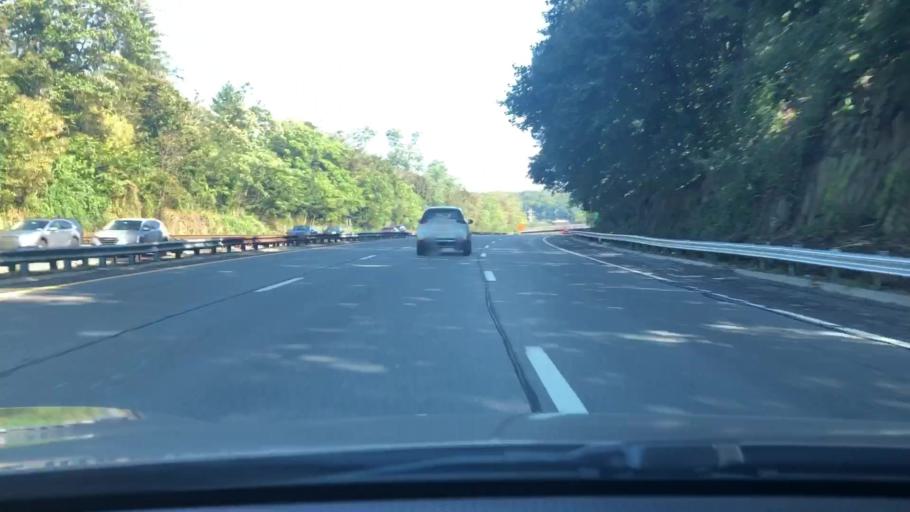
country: US
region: New York
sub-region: Westchester County
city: Elmsford
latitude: 41.0451
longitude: -73.8148
